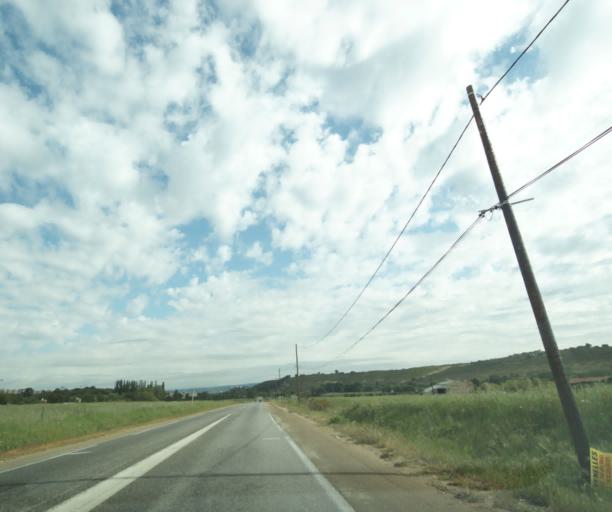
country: FR
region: Provence-Alpes-Cote d'Azur
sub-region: Departement des Bouches-du-Rhone
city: Cabries
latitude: 43.4698
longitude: 5.3545
